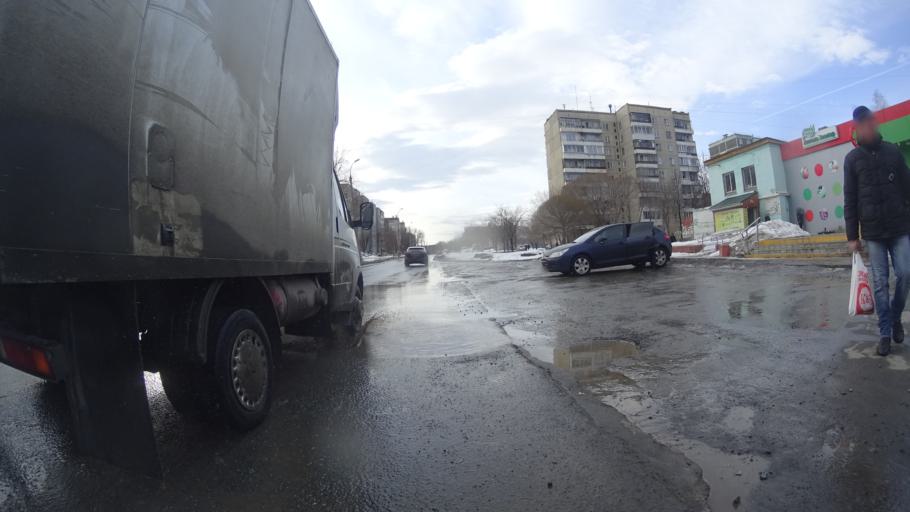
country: RU
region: Chelyabinsk
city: Roshchino
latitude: 55.1988
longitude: 61.3139
